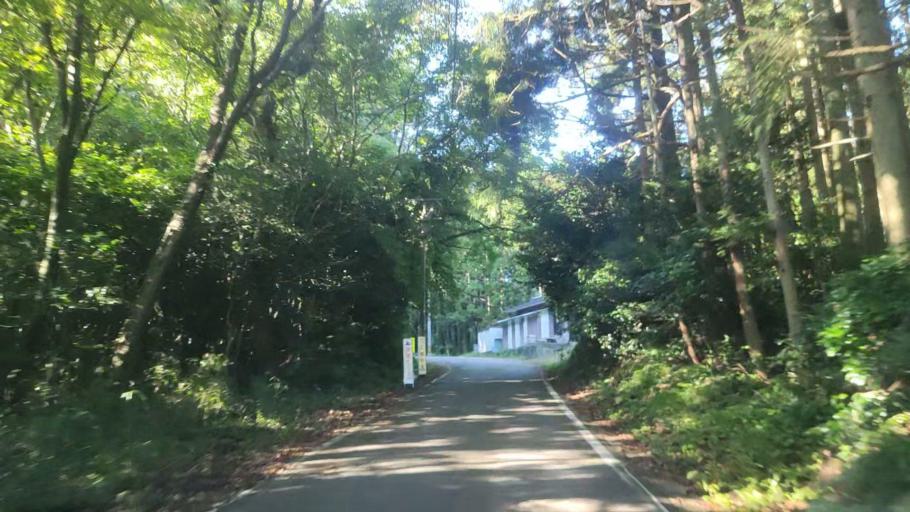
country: JP
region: Ishikawa
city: Nanao
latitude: 37.1295
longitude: 136.8941
